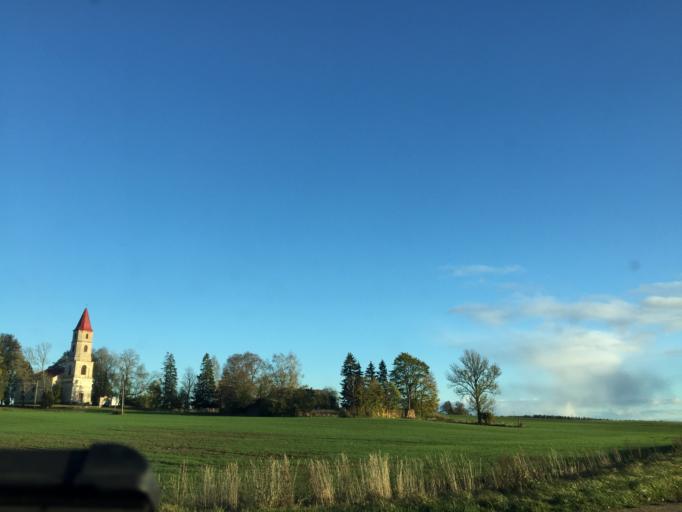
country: LV
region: Saldus Rajons
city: Saldus
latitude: 56.8125
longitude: 22.3808
